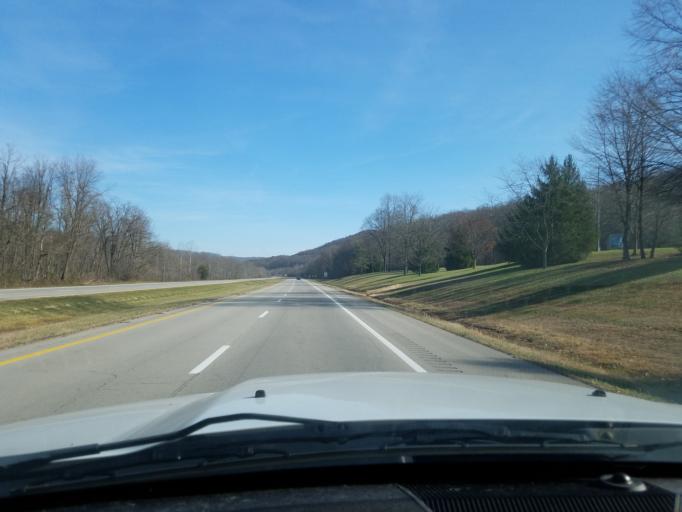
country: US
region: Ohio
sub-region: Adams County
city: Peebles
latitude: 39.0422
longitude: -83.2300
